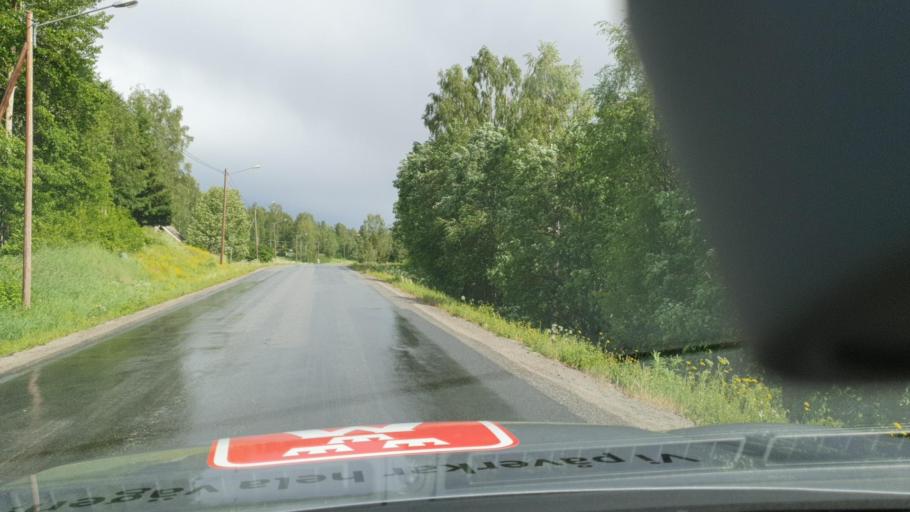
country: SE
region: Vaesternorrland
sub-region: OErnskoeldsviks Kommun
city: Bredbyn
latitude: 63.3302
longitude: 18.2375
